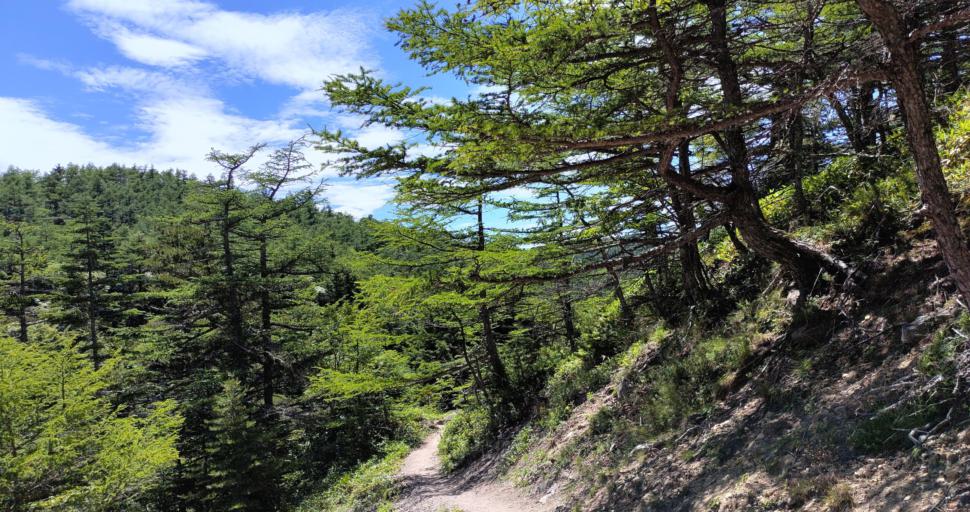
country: JP
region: Nagano
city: Komoro
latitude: 36.4056
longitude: 138.4770
